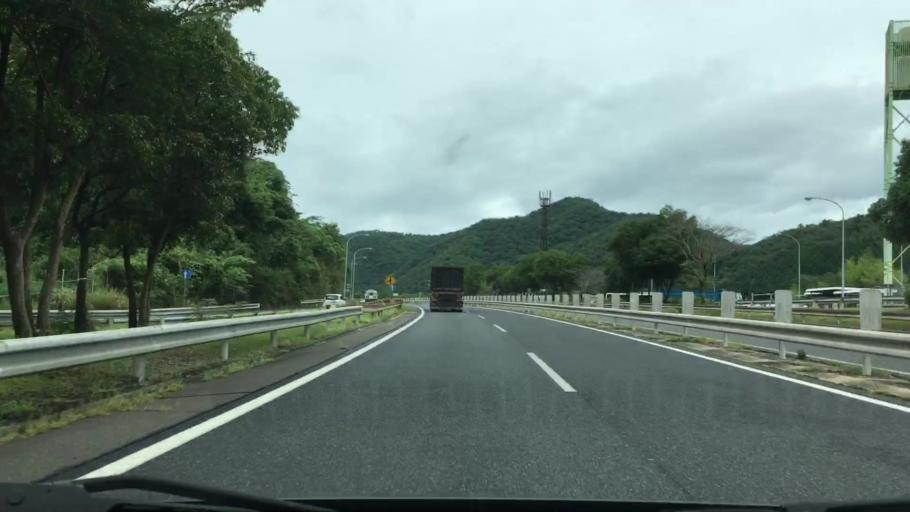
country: JP
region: Hyogo
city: Yamazakicho-nakabirose
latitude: 35.0100
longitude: 134.3080
